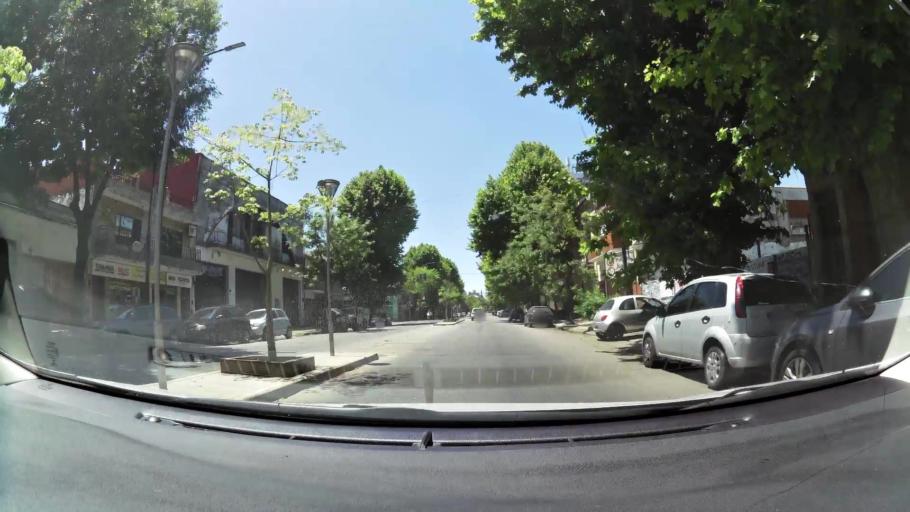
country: AR
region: Buenos Aires
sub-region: Partido de Avellaneda
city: Avellaneda
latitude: -34.6501
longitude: -58.3832
